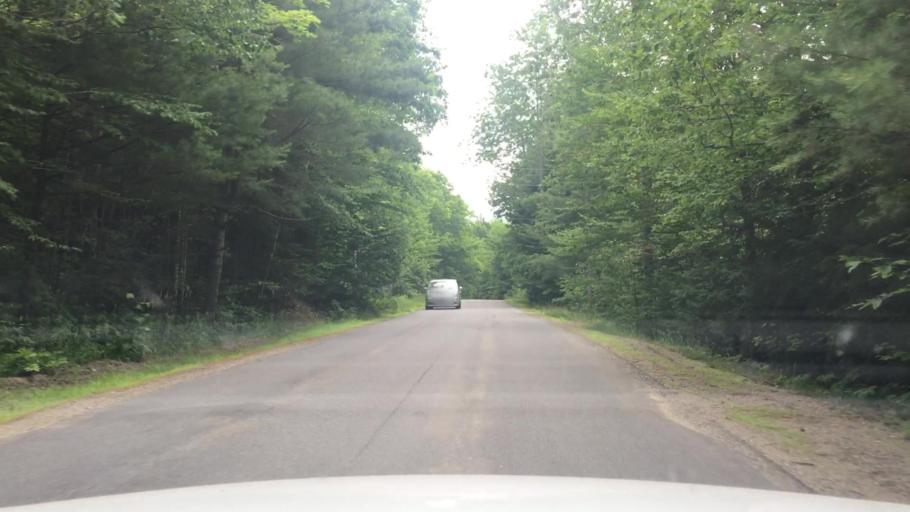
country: US
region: Maine
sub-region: Kennebec County
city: Albion
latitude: 44.4534
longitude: -69.3165
